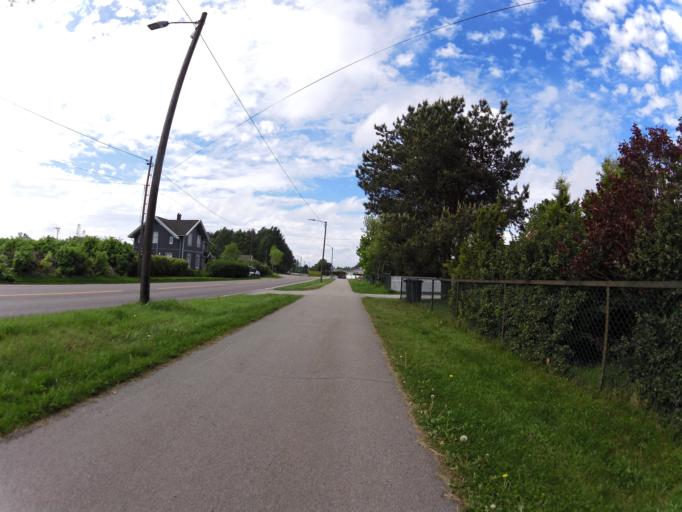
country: NO
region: Ostfold
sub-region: Rade
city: Karlshus
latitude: 59.3481
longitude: 10.8905
